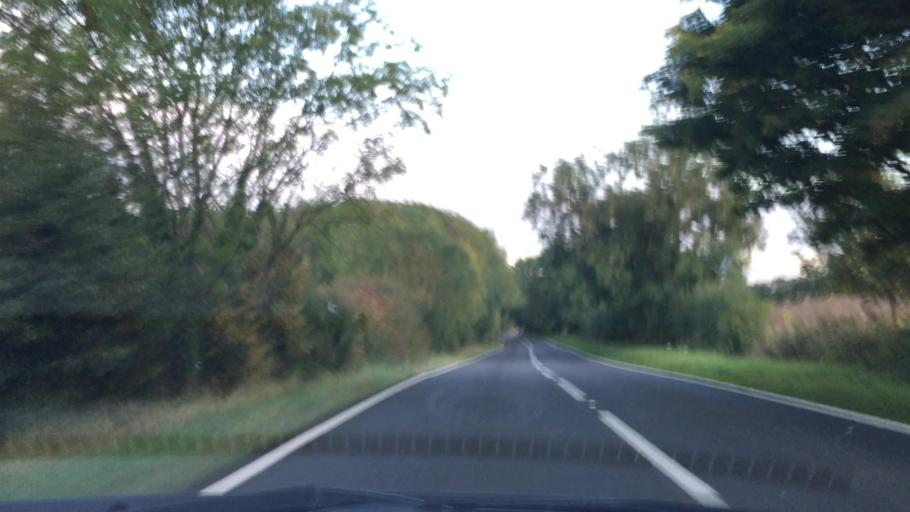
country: GB
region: England
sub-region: North East Lincolnshire
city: Wold Newton
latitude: 53.4751
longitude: -0.1149
